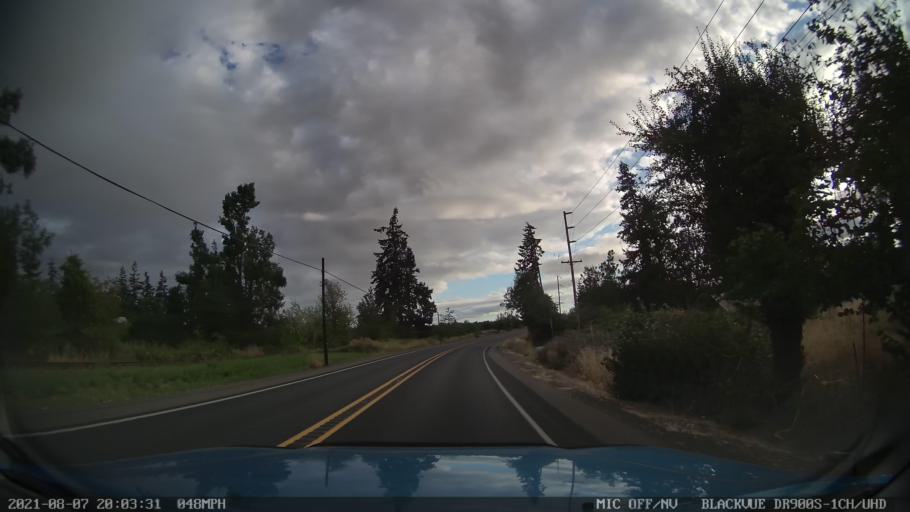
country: US
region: Oregon
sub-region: Marion County
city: Silverton
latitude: 44.9959
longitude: -122.8177
